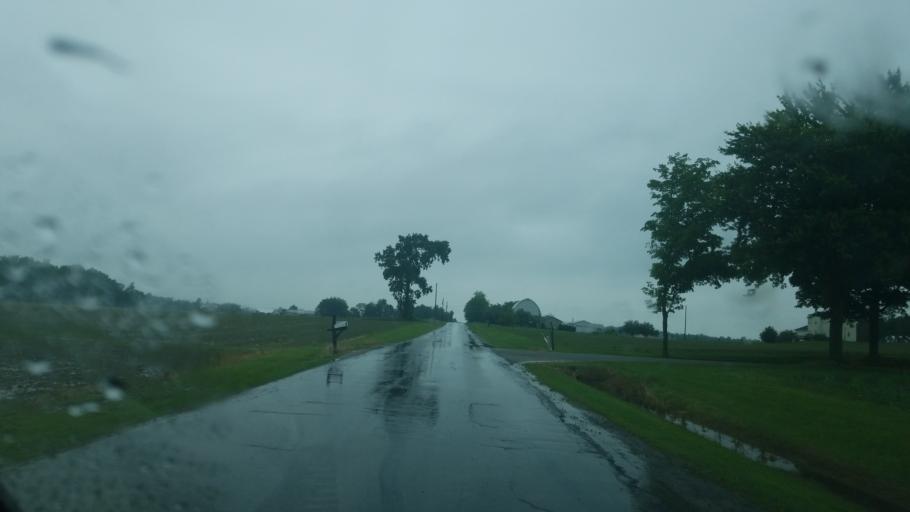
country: US
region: Ohio
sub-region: Huron County
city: Plymouth
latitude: 40.9861
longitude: -82.6054
